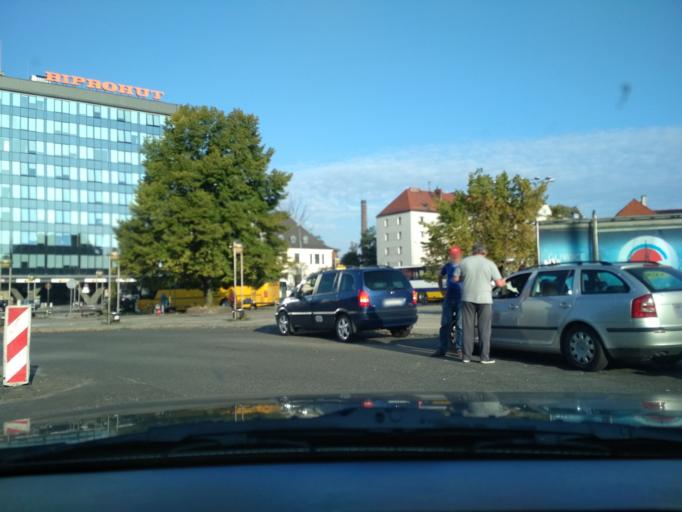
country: PL
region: Silesian Voivodeship
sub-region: Gliwice
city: Gliwice
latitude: 50.3003
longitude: 18.6765
